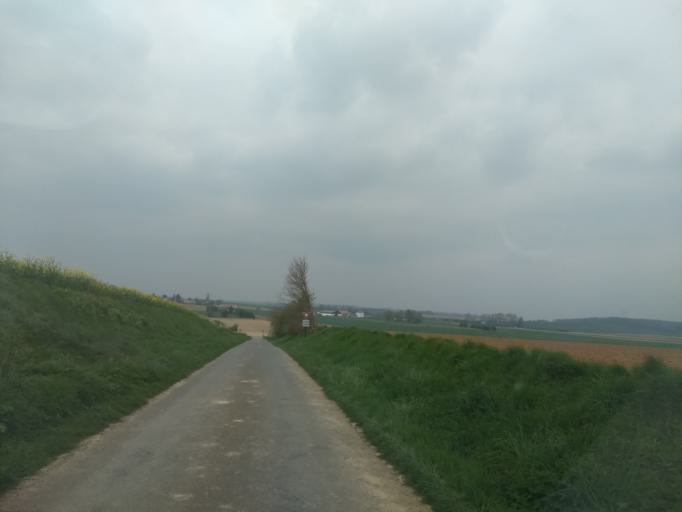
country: FR
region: Nord-Pas-de-Calais
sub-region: Departement du Pas-de-Calais
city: Mont-Saint-Eloi
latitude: 50.3451
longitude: 2.7014
